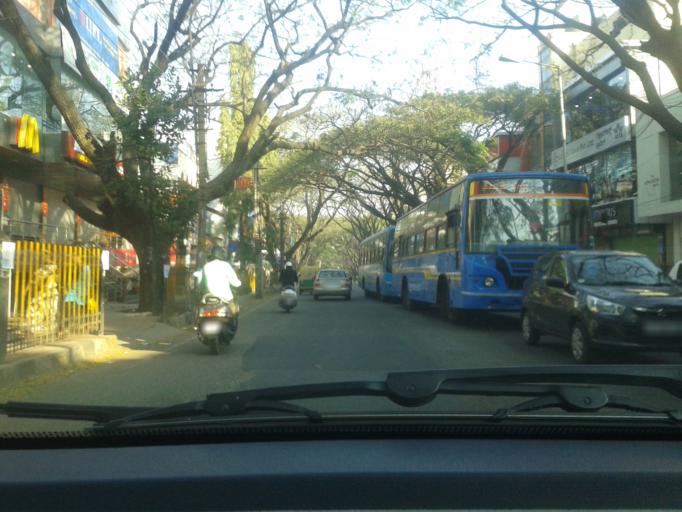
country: IN
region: Karnataka
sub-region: Bangalore Urban
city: Bangalore
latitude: 13.0291
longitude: 77.5710
